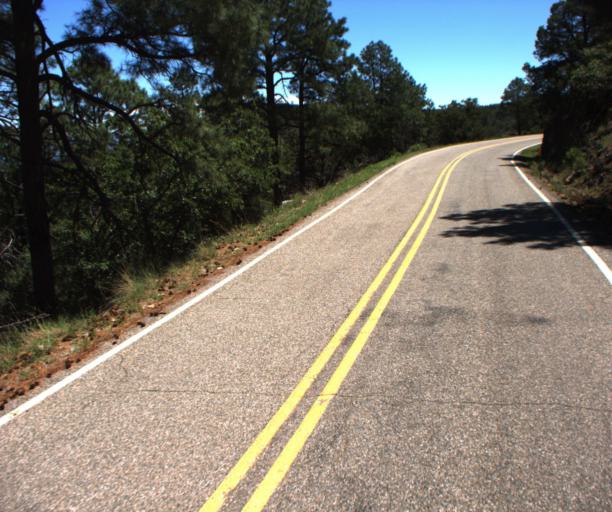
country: US
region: Arizona
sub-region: Greenlee County
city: Morenci
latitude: 33.2512
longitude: -109.3708
